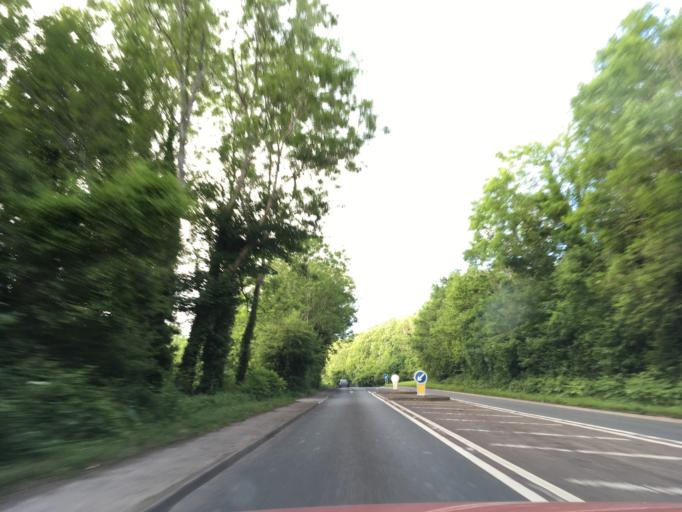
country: GB
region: England
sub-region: Somerset
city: Axbridge
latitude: 51.2952
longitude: -2.8301
